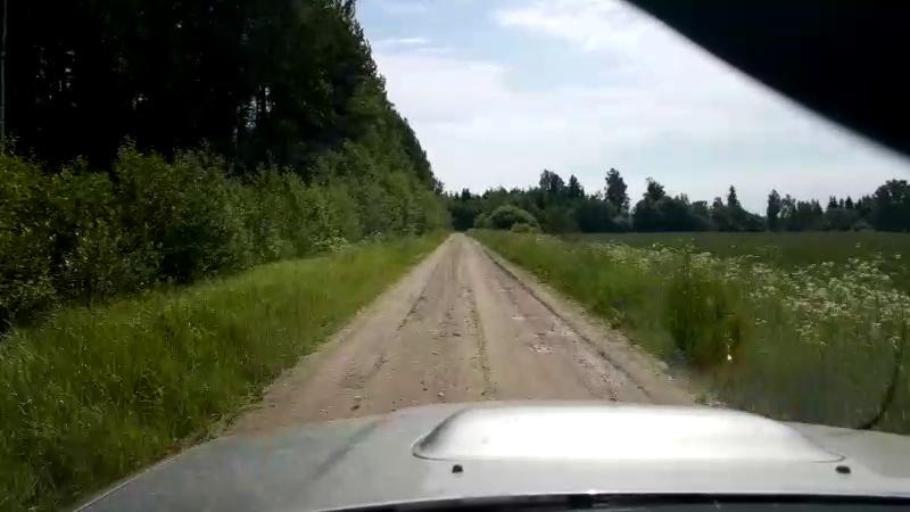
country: EE
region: Paernumaa
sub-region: Sindi linn
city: Sindi
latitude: 58.5301
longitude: 24.6708
